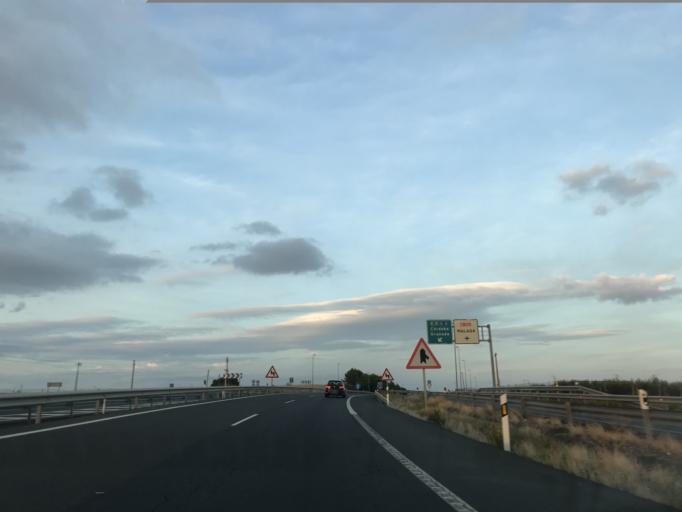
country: ES
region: Andalusia
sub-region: Province of Cordoba
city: La Victoria
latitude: 37.7586
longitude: -4.8282
